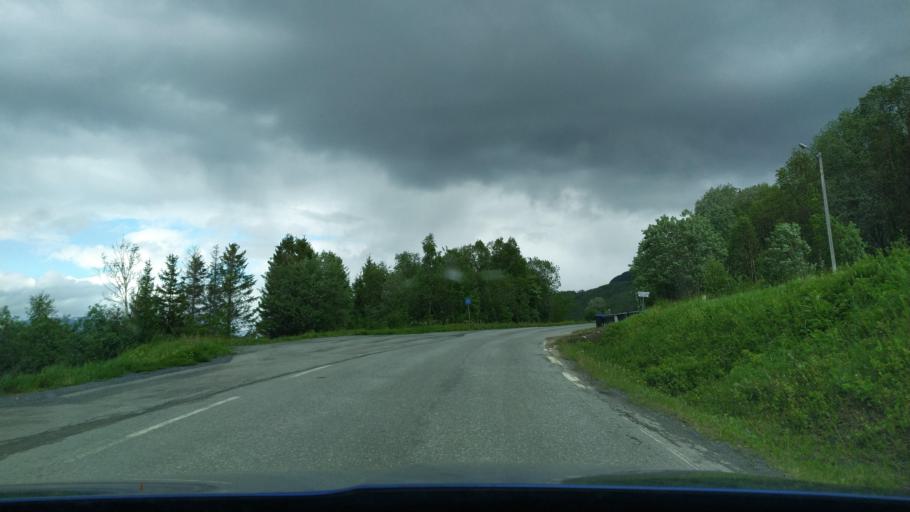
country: NO
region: Troms
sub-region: Lenvik
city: Finnsnes
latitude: 69.1314
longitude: 17.8748
